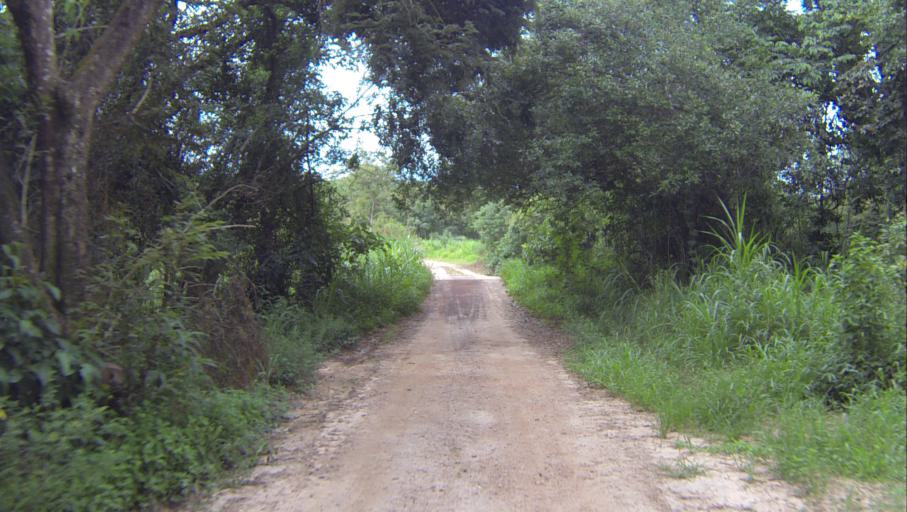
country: BR
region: Minas Gerais
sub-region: Brumadinho
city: Brumadinho
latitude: -20.1598
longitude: -44.1300
